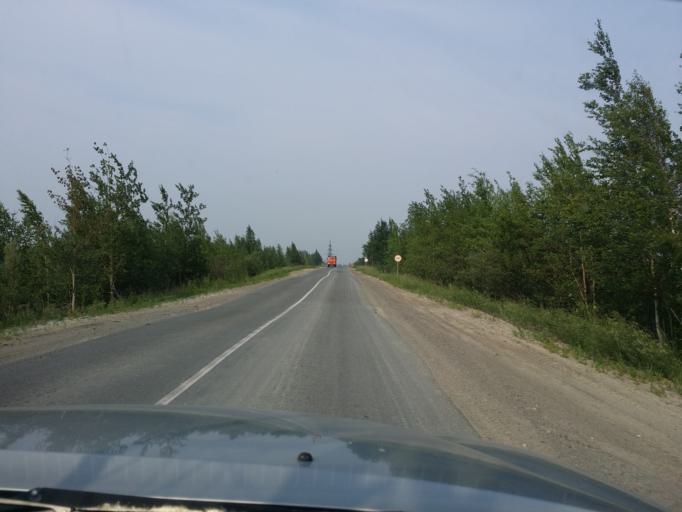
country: RU
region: Khanty-Mansiyskiy Avtonomnyy Okrug
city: Nizhnevartovsk
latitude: 61.0826
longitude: 76.6570
